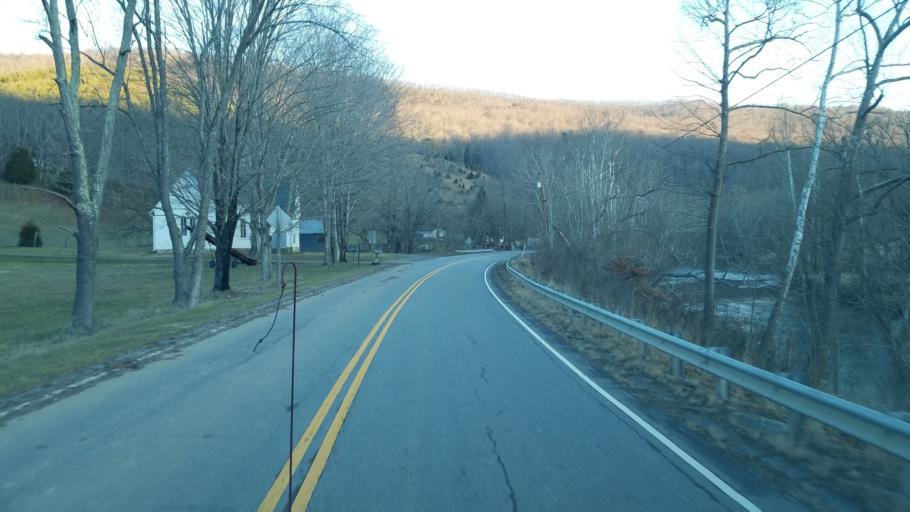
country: US
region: Virginia
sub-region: Giles County
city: Narrows
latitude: 37.1936
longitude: -80.8382
